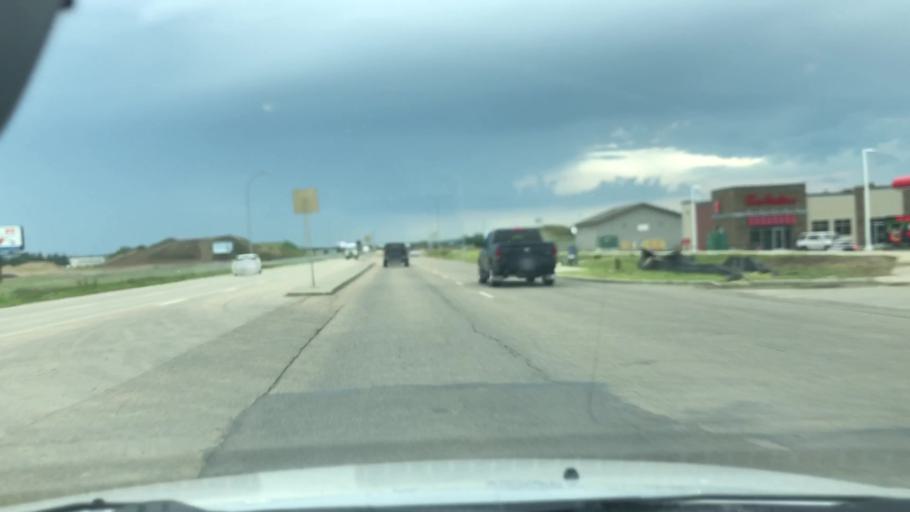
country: CA
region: Alberta
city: St. Albert
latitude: 53.5994
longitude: -113.6048
